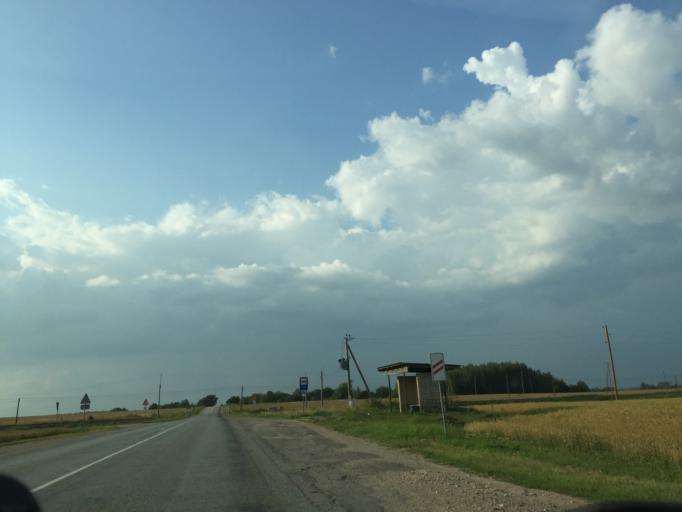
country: LV
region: Dobeles Rajons
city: Dobele
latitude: 56.5485
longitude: 23.3110
